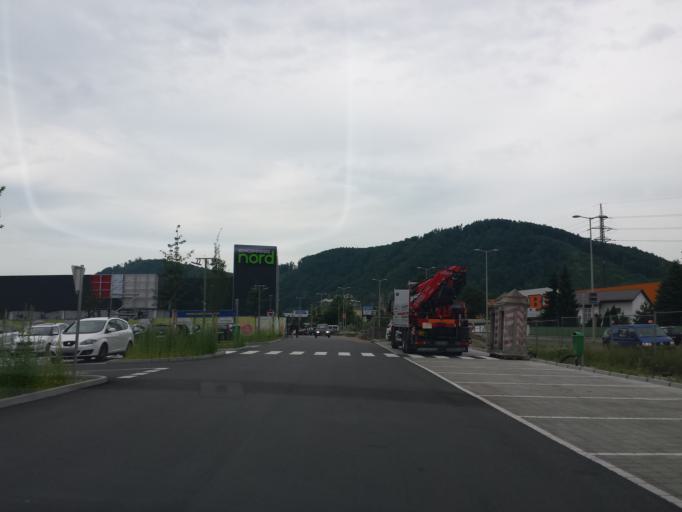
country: AT
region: Styria
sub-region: Graz Stadt
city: Goesting
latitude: 47.1031
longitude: 15.4022
